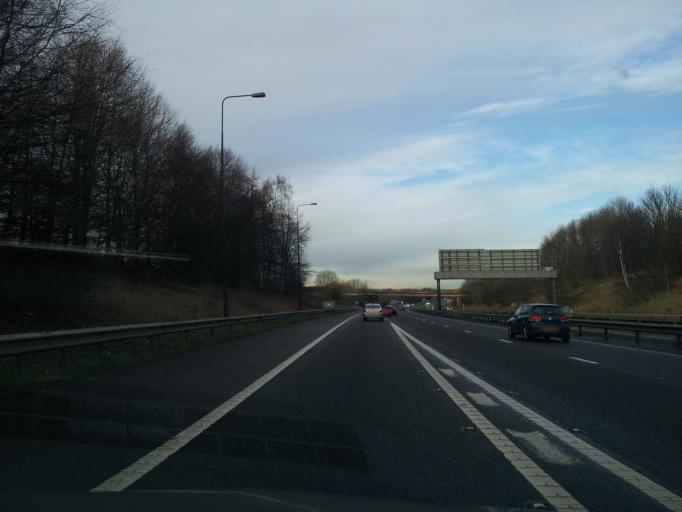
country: GB
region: England
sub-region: Borough of Bury
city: Prestwich
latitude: 53.5558
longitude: -2.2664
